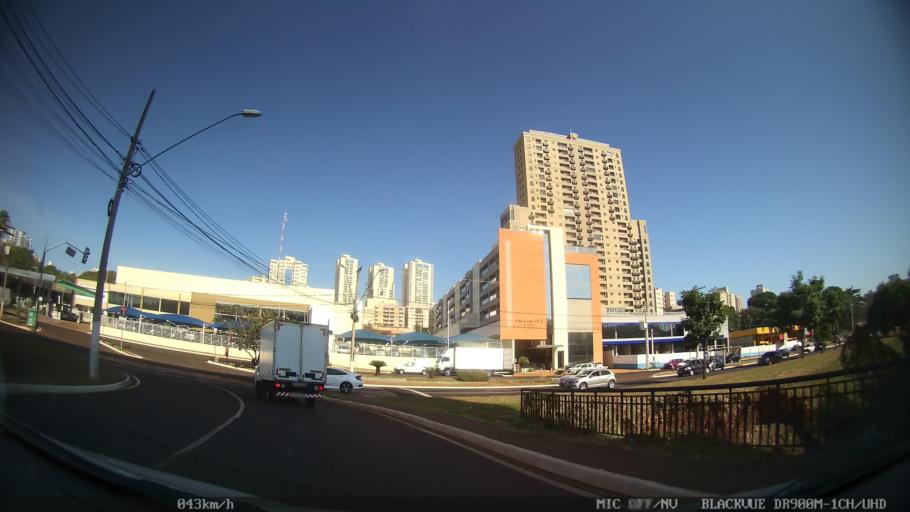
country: BR
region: Sao Paulo
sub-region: Ribeirao Preto
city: Ribeirao Preto
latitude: -21.2062
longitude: -47.7915
